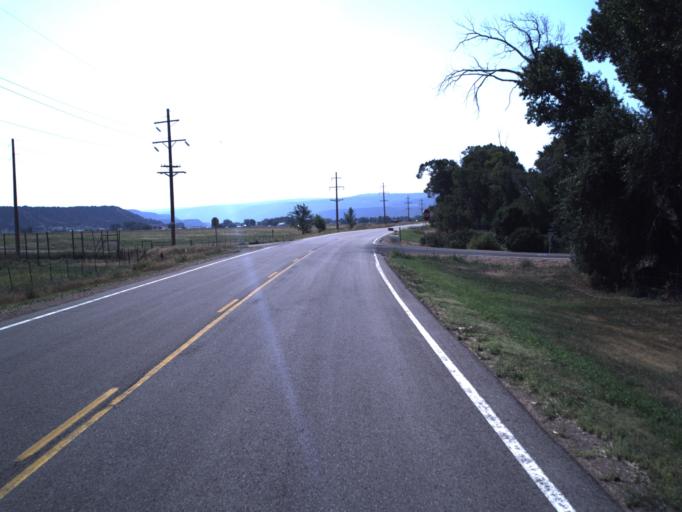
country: US
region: Utah
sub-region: Duchesne County
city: Duchesne
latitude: 40.3719
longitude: -110.7275
